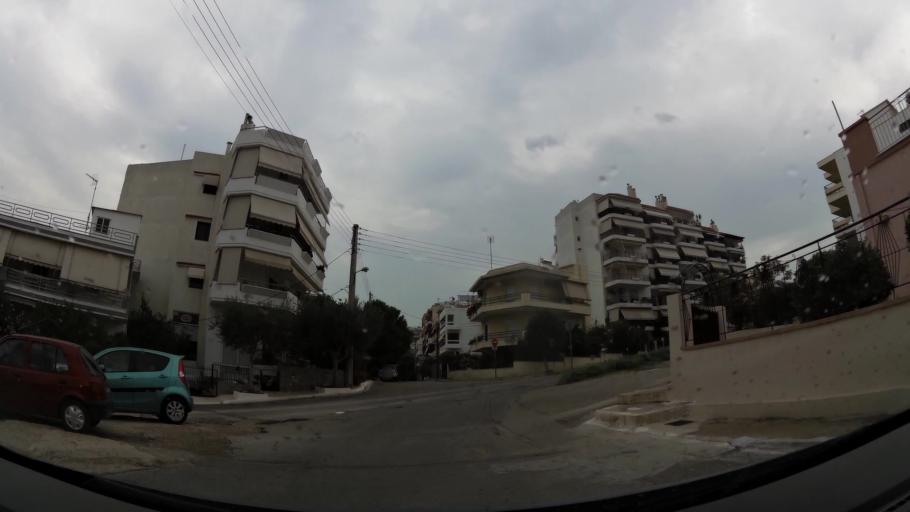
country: GR
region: Attica
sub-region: Nomarchia Athinas
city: Alimos
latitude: 37.9211
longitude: 23.7196
